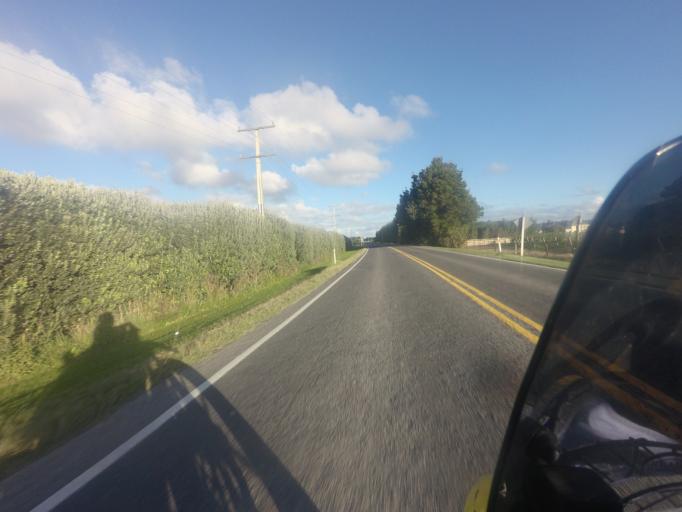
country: NZ
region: Gisborne
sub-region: Gisborne District
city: Gisborne
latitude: -38.6012
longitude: 177.9613
